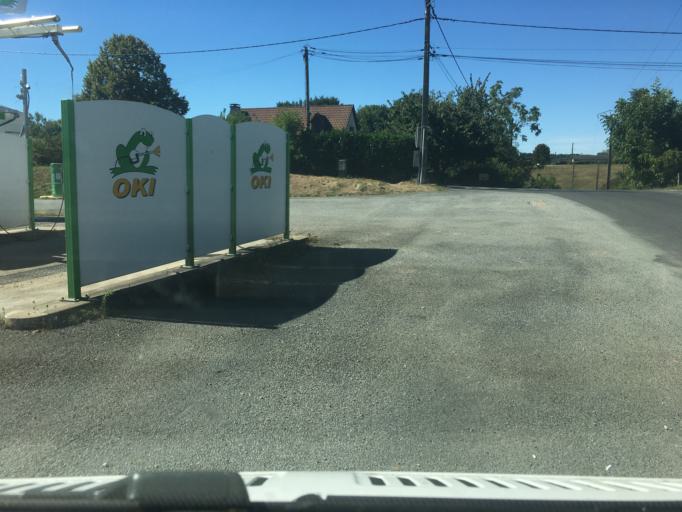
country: FR
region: Limousin
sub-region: Departement de la Correze
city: Bort-les-Orgues
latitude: 45.4263
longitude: 2.5061
